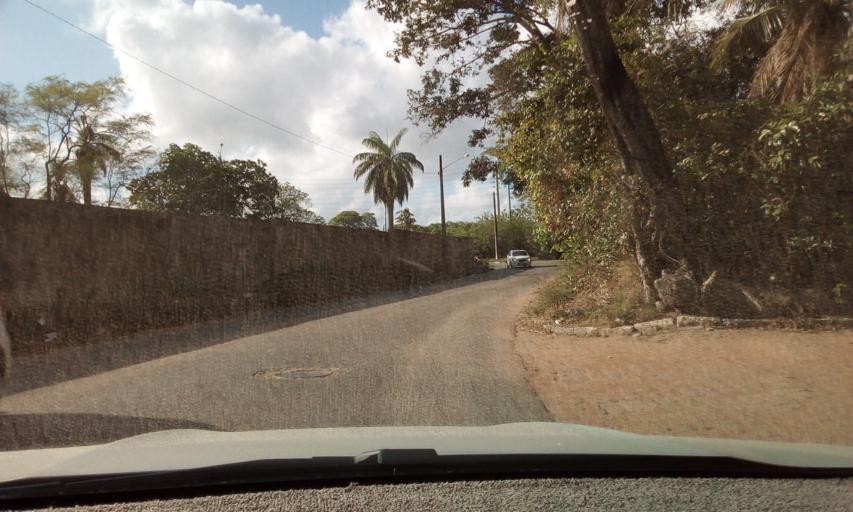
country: BR
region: Paraiba
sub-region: Bayeux
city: Bayeux
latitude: -7.1470
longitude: -34.9074
